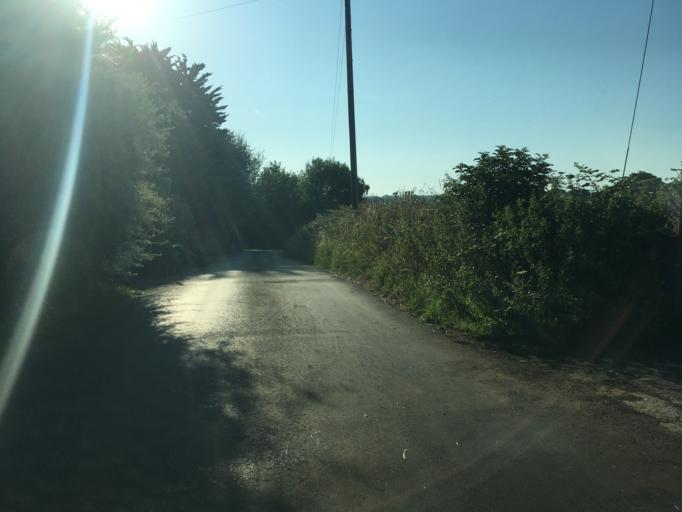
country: GB
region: England
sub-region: South Gloucestershire
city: Winterbourne
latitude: 51.5243
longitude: -2.4979
